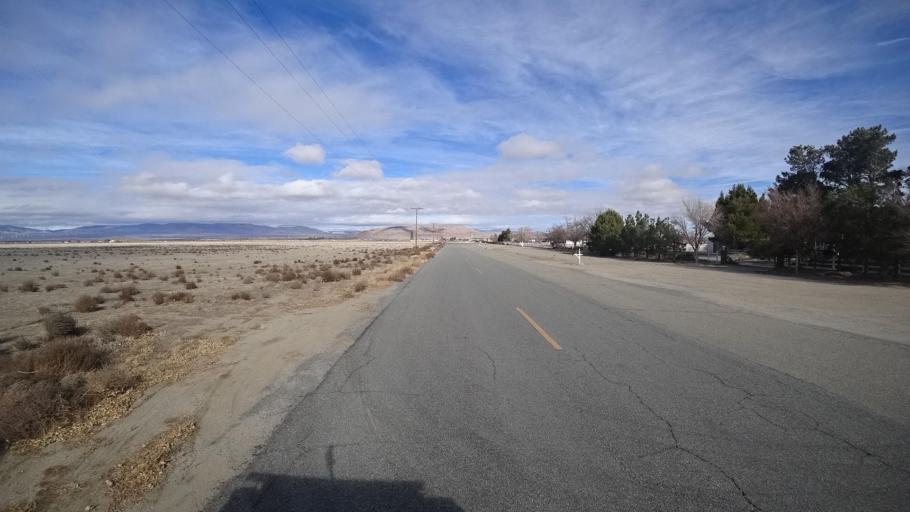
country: US
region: California
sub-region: Kern County
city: Rosamond
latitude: 34.8292
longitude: -118.2730
